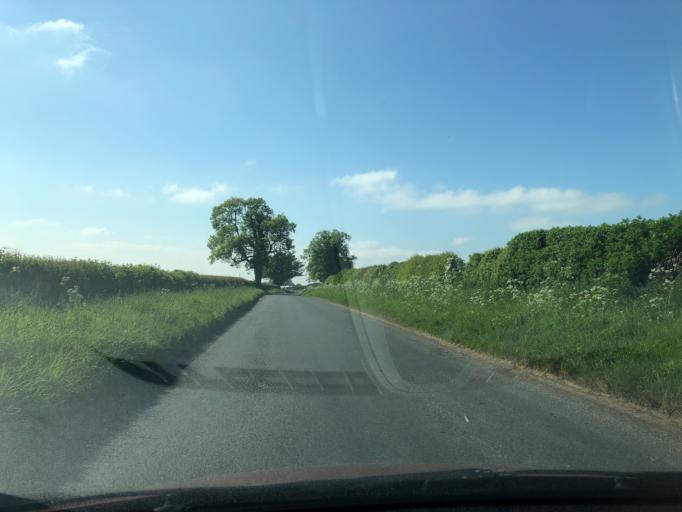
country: GB
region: England
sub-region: North Yorkshire
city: Northallerton
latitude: 54.3298
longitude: -1.4105
